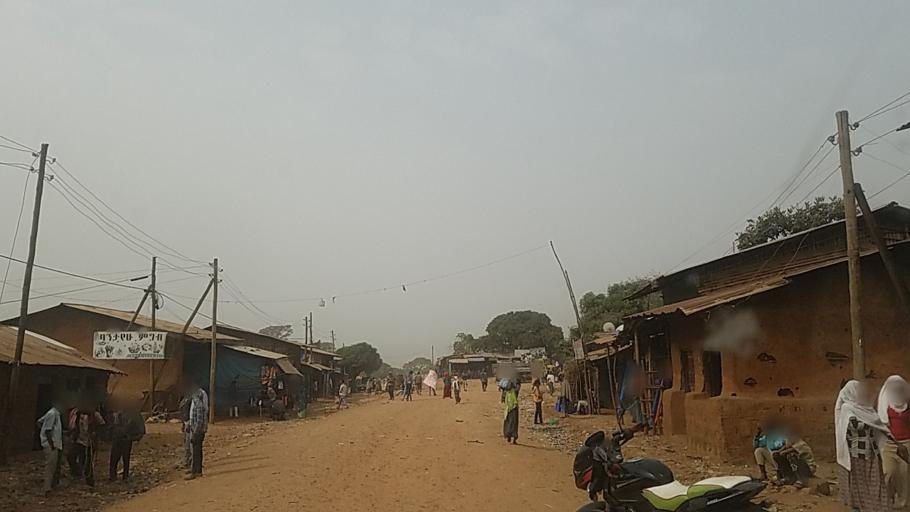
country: ET
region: Amhara
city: Bure
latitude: 10.8477
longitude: 36.3458
